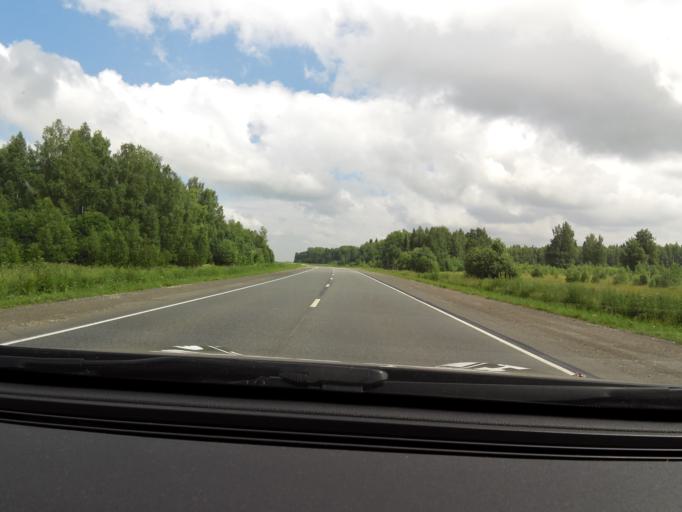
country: RU
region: Perm
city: Ust'-Kishert'
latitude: 57.1594
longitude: 57.1667
